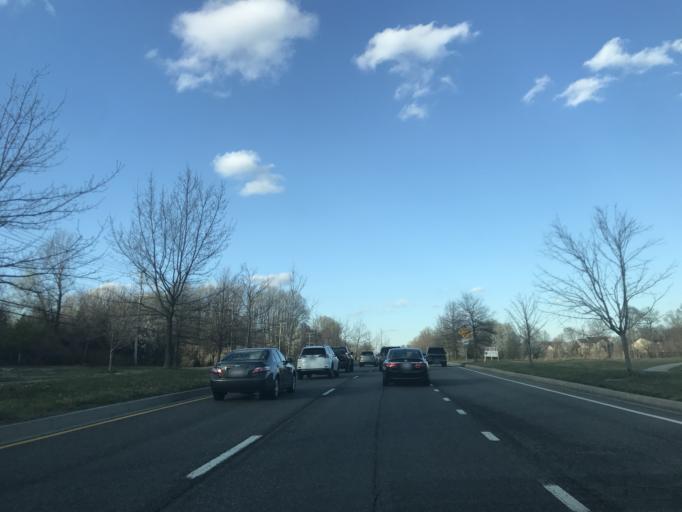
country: US
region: Maryland
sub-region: Prince George's County
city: Glenn Dale
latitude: 38.9667
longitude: -76.7913
